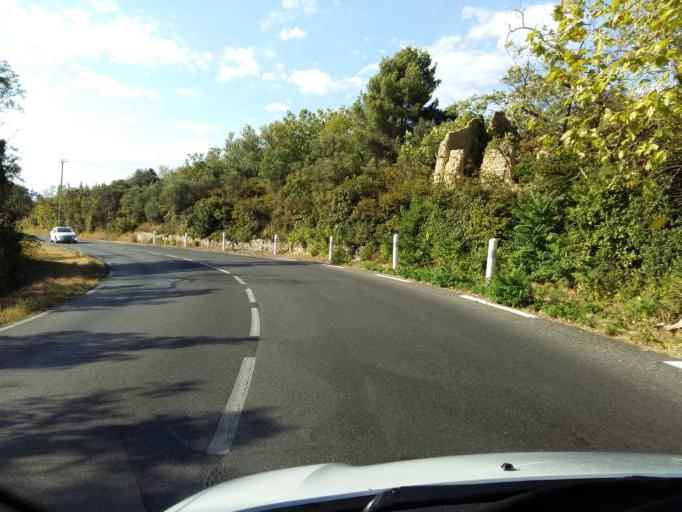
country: FR
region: Provence-Alpes-Cote d'Azur
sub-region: Departement du Vaucluse
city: Jonquerettes
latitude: 43.9344
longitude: 4.9220
